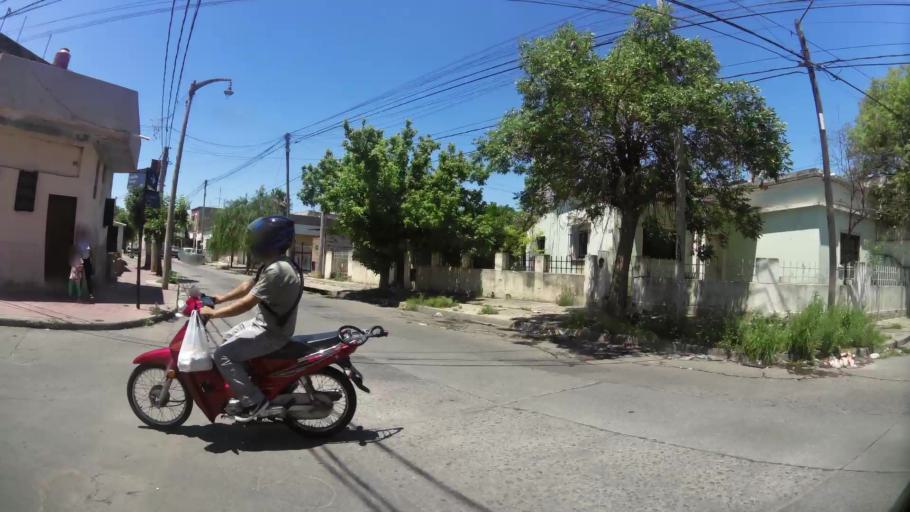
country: AR
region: Cordoba
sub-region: Departamento de Capital
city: Cordoba
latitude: -31.3989
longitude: -64.2064
